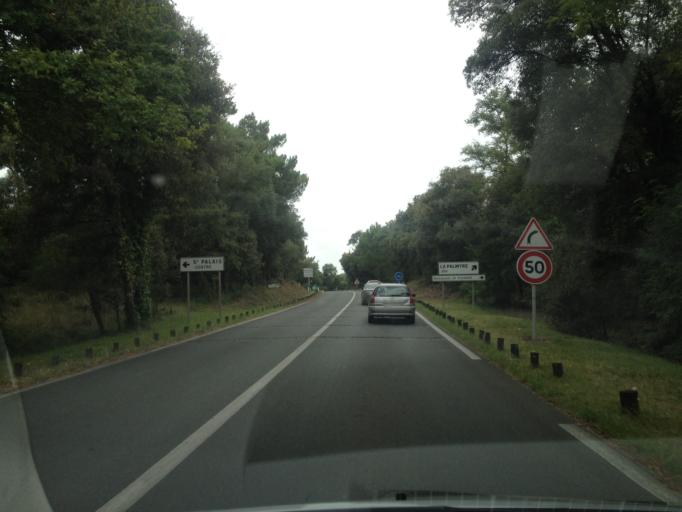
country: FR
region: Poitou-Charentes
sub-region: Departement de la Charente-Maritime
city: Saint-Palais-sur-Mer
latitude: 45.6583
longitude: -1.1248
